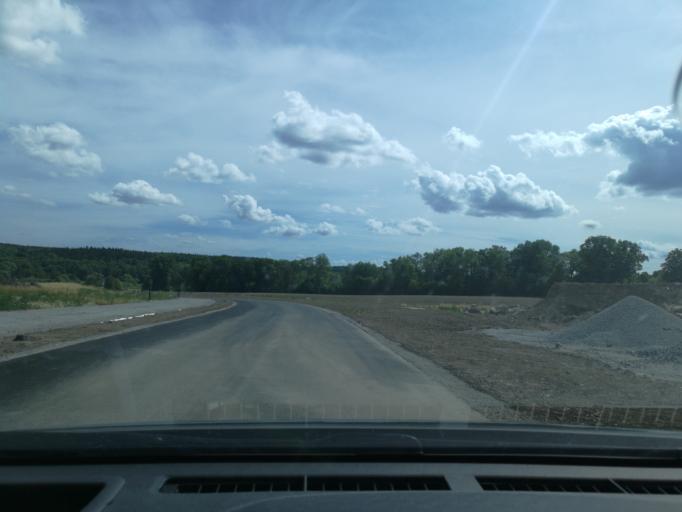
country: SE
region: Stockholm
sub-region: Sigtuna Kommun
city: Marsta
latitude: 59.6057
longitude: 17.8043
